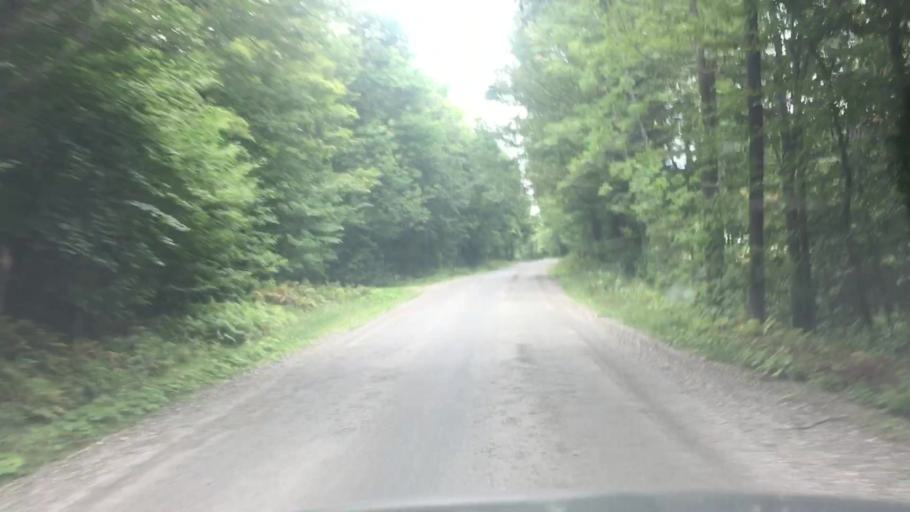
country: US
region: Vermont
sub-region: Windham County
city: Dover
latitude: 42.8358
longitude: -72.8049
